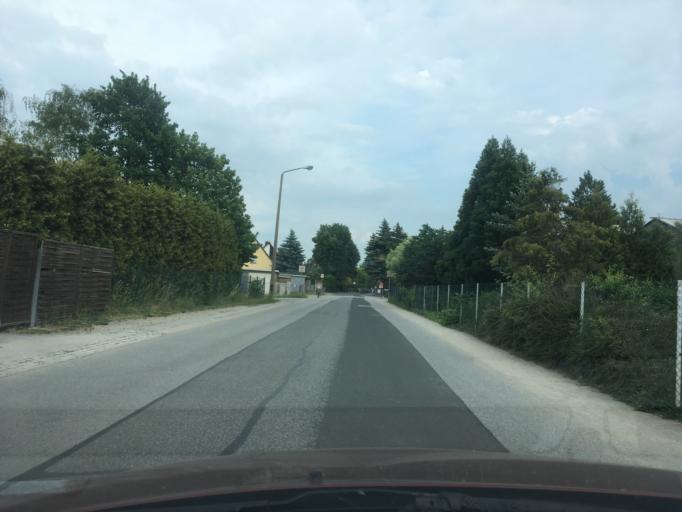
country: DE
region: Saxony
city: Bautzen
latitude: 51.1718
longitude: 14.4447
